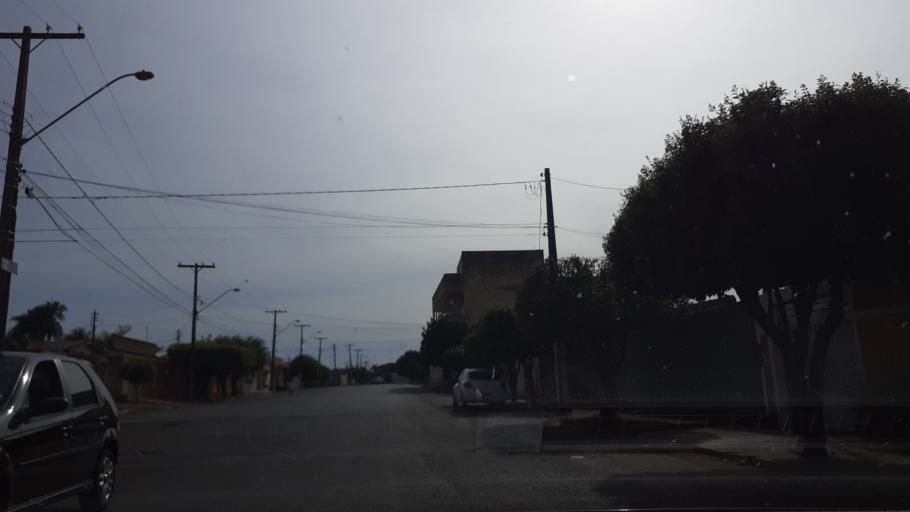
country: BR
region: Goias
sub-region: Itumbiara
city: Itumbiara
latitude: -18.4185
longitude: -49.2419
